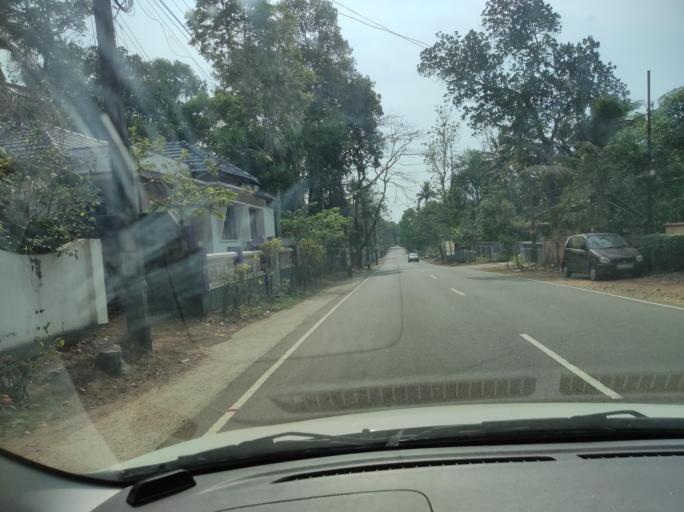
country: IN
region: Kerala
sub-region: Kottayam
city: Kottayam
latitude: 9.6752
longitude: 76.5371
